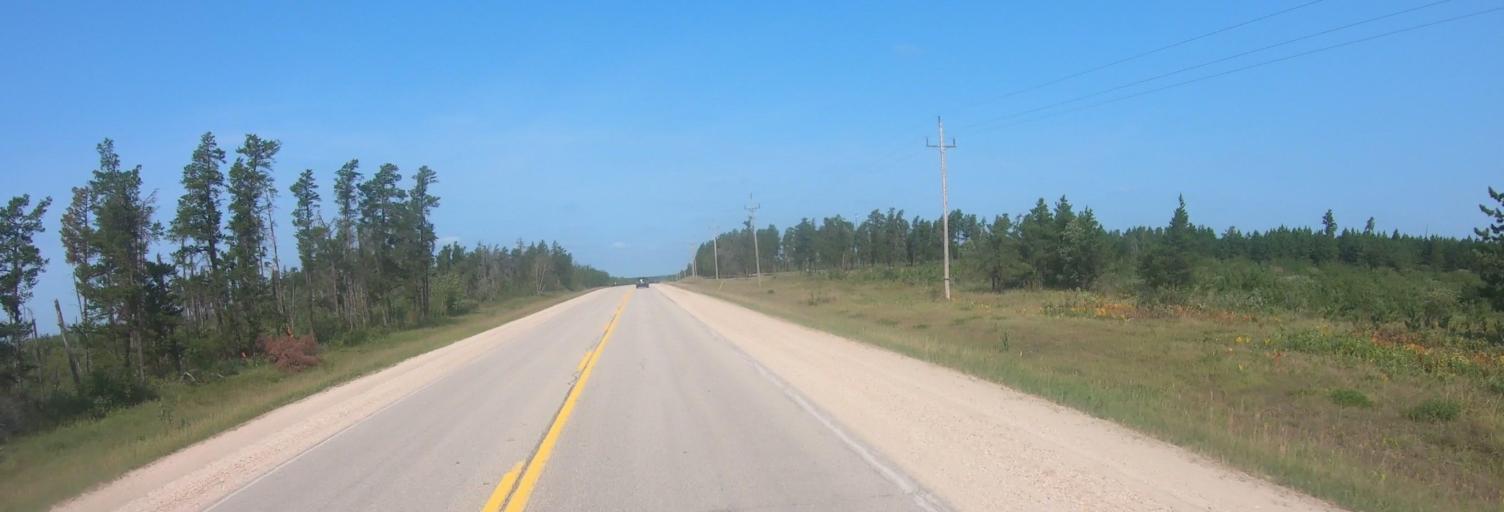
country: US
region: Minnesota
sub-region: Roseau County
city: Roseau
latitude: 49.1320
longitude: -96.0843
